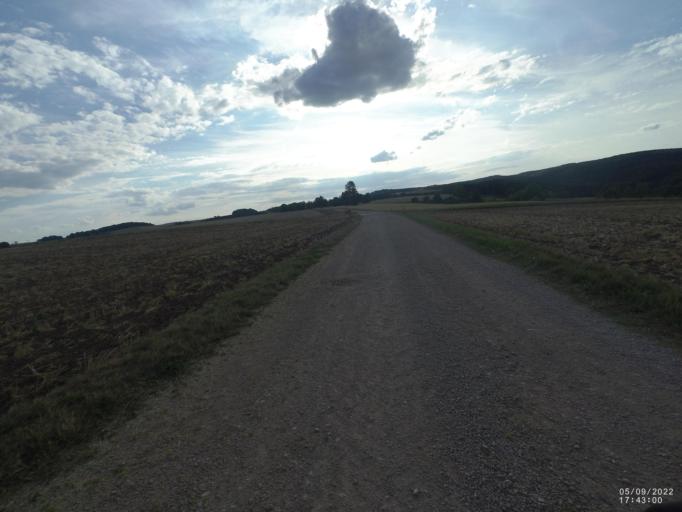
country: DE
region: Rheinland-Pfalz
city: Basberg
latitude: 50.3035
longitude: 6.6024
